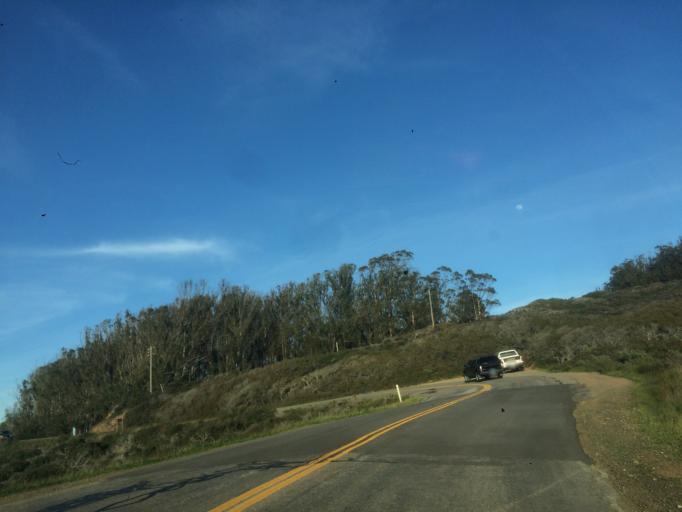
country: US
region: California
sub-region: San Luis Obispo County
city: Los Osos
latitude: 35.2993
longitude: -120.8638
